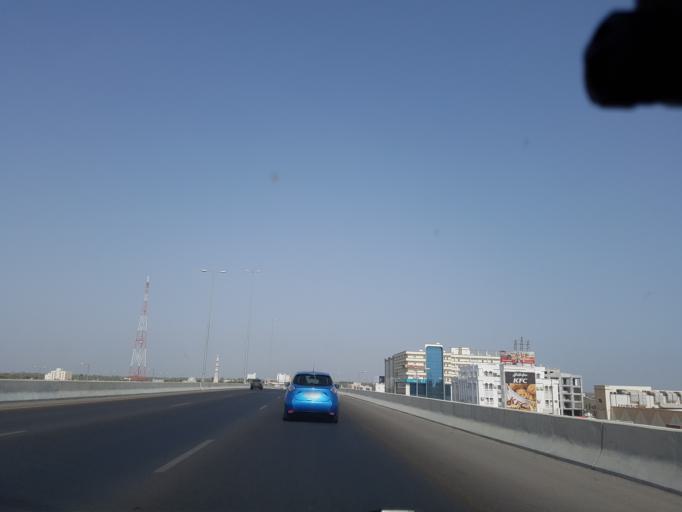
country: OM
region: Al Batinah
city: Barka'
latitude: 23.6674
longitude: 57.8834
